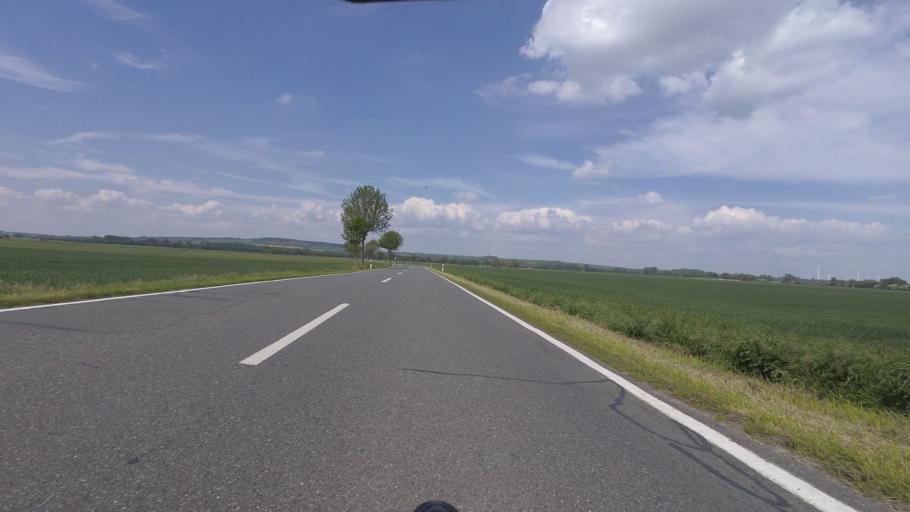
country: DE
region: Lower Saxony
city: Jerxheim
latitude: 52.0496
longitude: 10.8839
